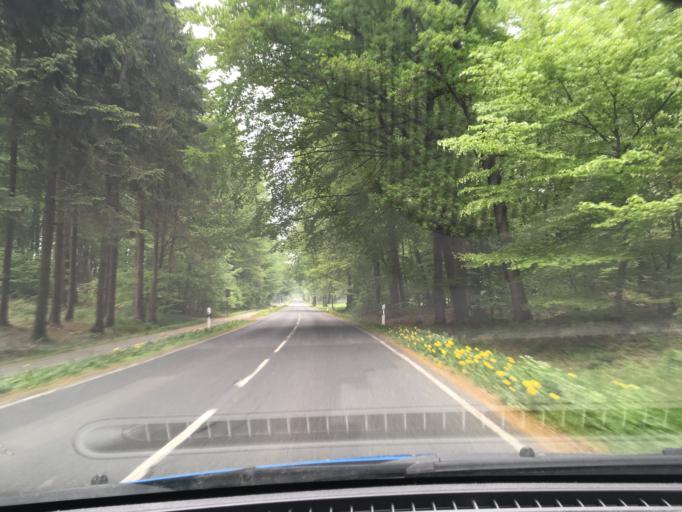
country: DE
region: Lower Saxony
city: Buchholz in der Nordheide
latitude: 53.4019
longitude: 9.8712
